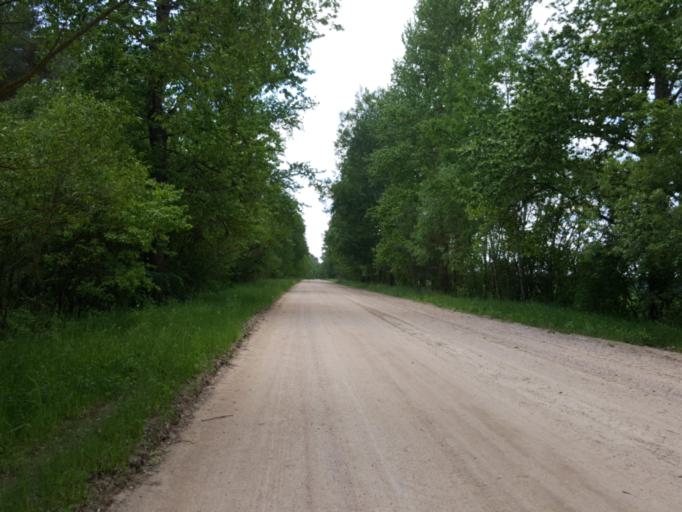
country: BY
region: Brest
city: Kamyanyuki
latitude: 52.5228
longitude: 23.6742
